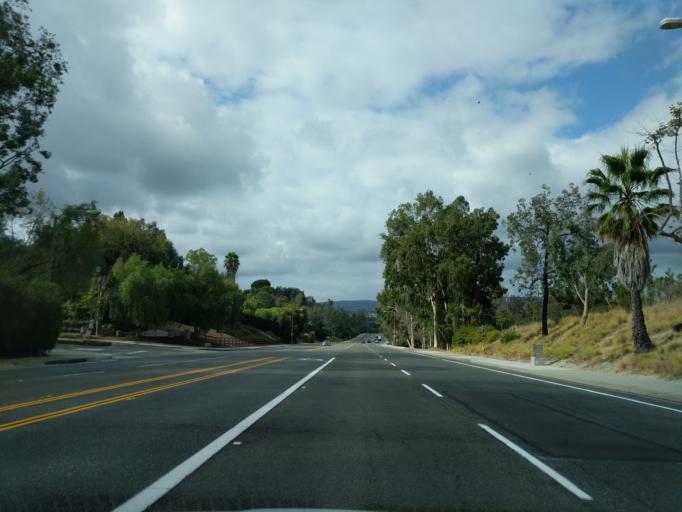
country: US
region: California
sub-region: Orange County
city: Mission Viejo
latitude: 33.5823
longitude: -117.6928
